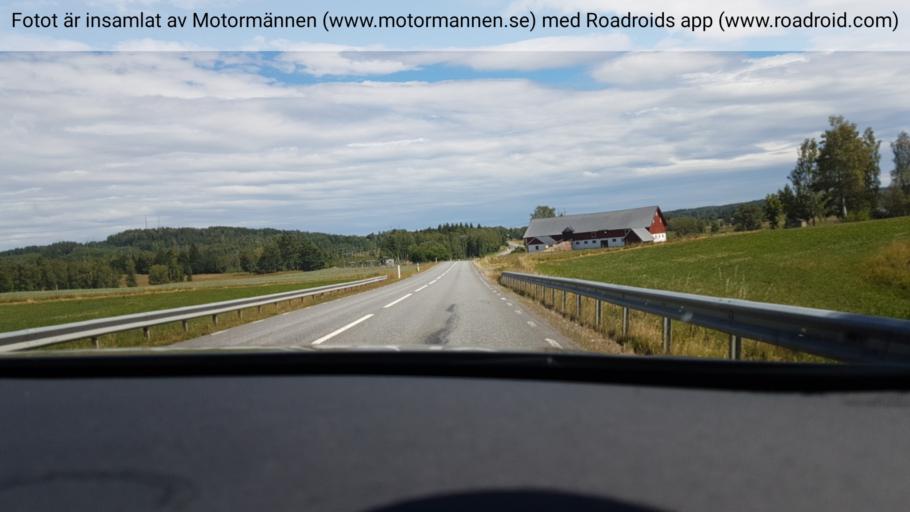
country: SE
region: Joenkoeping
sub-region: Aneby Kommun
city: Aneby
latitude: 57.9771
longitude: 14.8133
